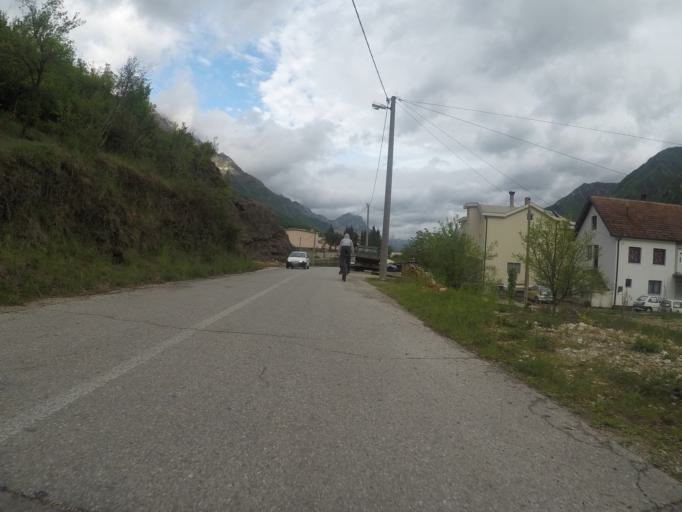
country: BA
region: Federation of Bosnia and Herzegovina
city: Siroki Brijeg
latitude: 43.5420
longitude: 17.5638
